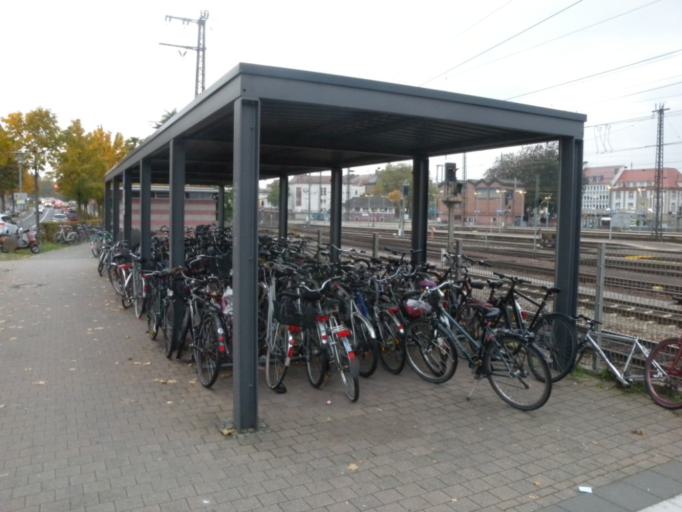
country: DE
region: Baden-Wuerttemberg
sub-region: Freiburg Region
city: Offenburg
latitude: 48.4753
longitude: 7.9469
